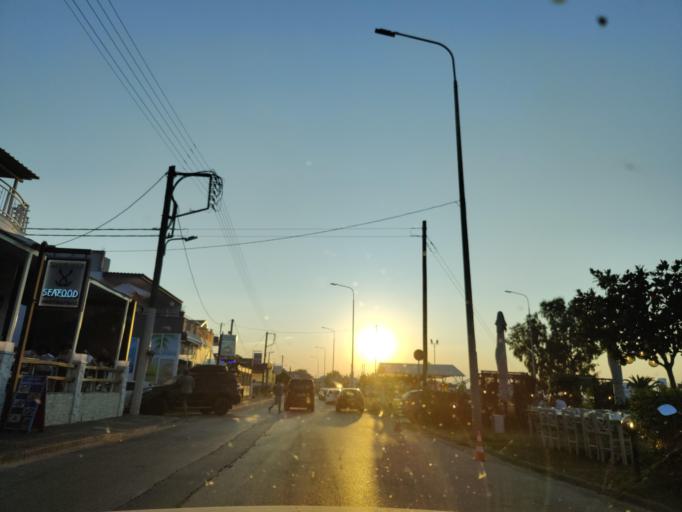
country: GR
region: East Macedonia and Thrace
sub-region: Nomos Kavalas
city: Keramoti
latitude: 40.8560
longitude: 24.7004
